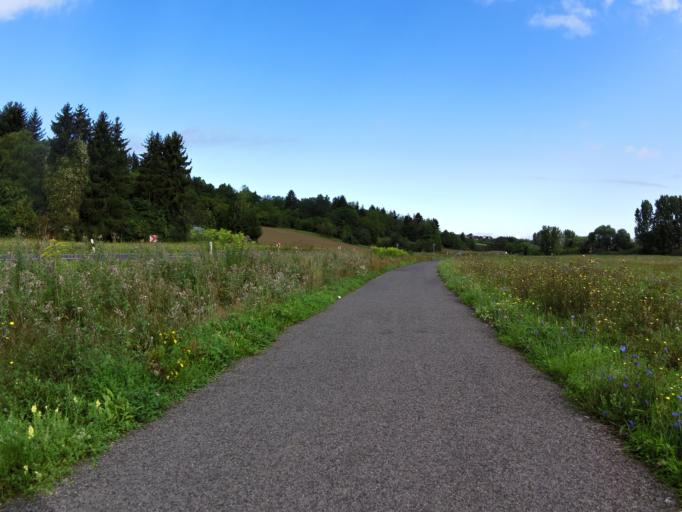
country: DE
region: Bavaria
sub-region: Regierungsbezirk Unterfranken
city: Buchbrunn
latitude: 49.7570
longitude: 10.1529
